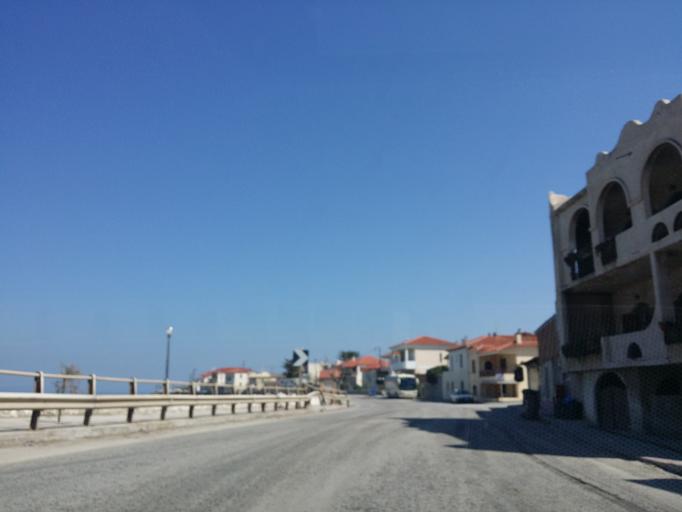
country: GR
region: West Greece
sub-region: Nomos Achaias
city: Aiyira
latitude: 38.1354
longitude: 22.4776
